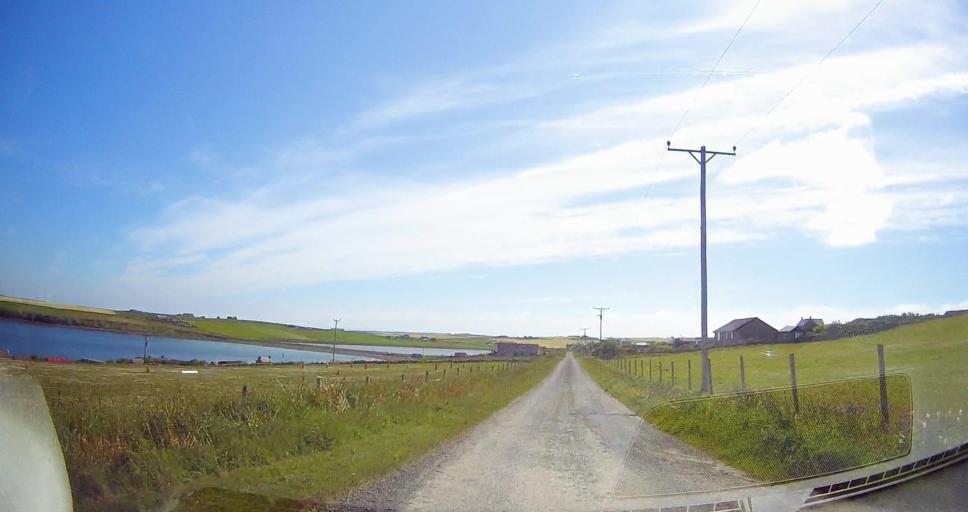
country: GB
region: Scotland
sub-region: Orkney Islands
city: Kirkwall
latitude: 58.8557
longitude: -2.9297
